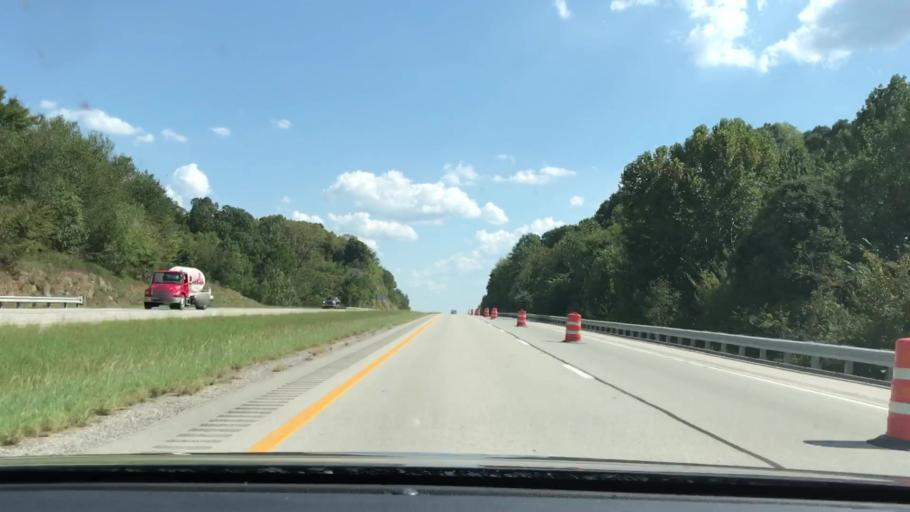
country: US
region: Kentucky
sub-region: Butler County
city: Morgantown
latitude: 37.2283
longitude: -86.7237
